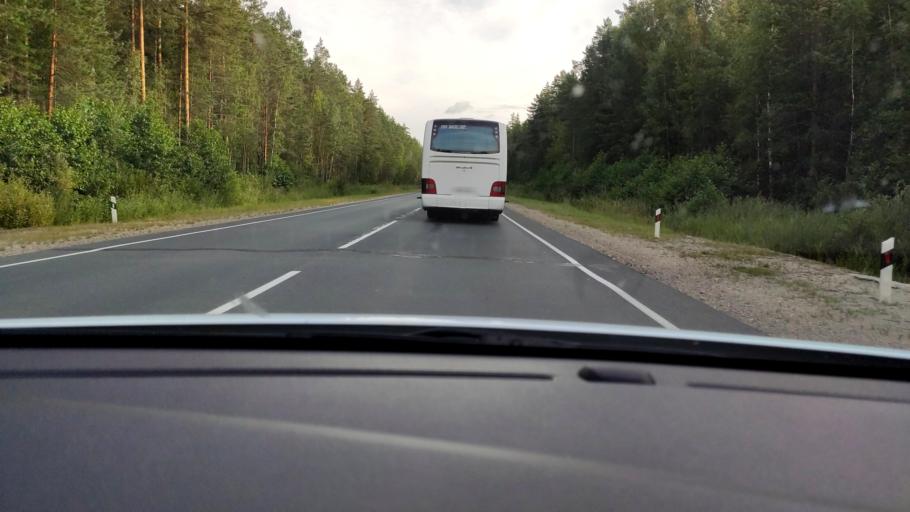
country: RU
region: Mariy-El
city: Suslonger
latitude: 56.2929
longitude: 48.2334
